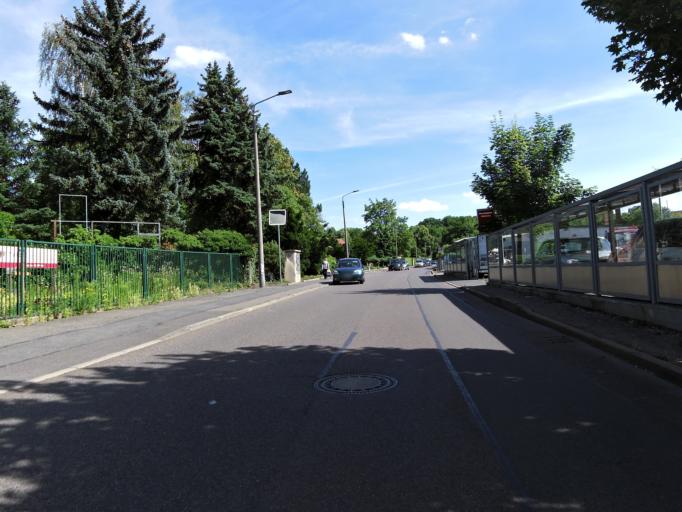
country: DE
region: Saxony
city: Leipzig
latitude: 51.3289
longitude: 12.4177
